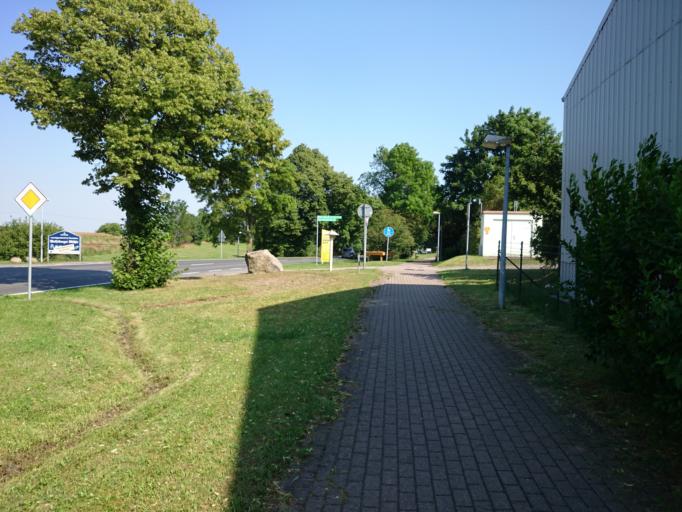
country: DE
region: Mecklenburg-Vorpommern
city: Tessin
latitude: 54.0339
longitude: 12.4428
